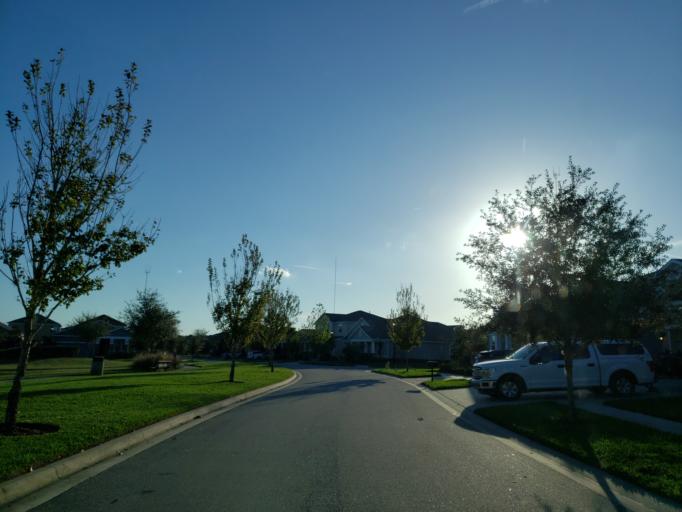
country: US
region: Florida
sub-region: Hillsborough County
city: Fish Hawk
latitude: 27.8488
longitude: -82.2504
